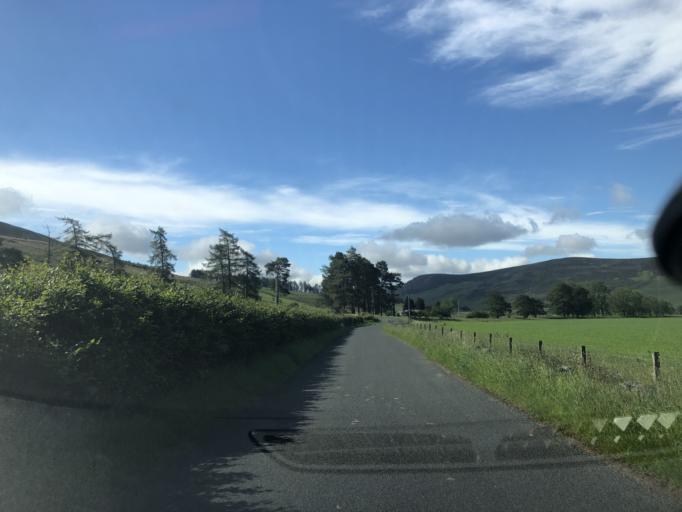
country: GB
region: Scotland
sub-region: Angus
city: Kirriemuir
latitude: 56.8119
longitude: -3.0336
